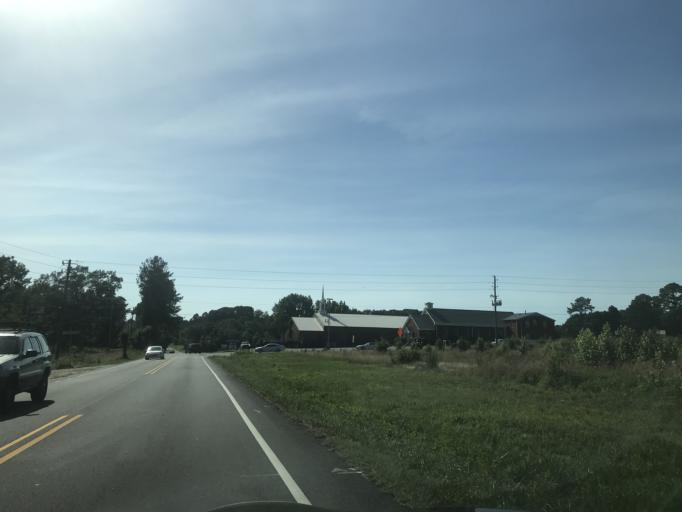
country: US
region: North Carolina
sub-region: Wake County
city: Garner
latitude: 35.6610
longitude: -78.5460
